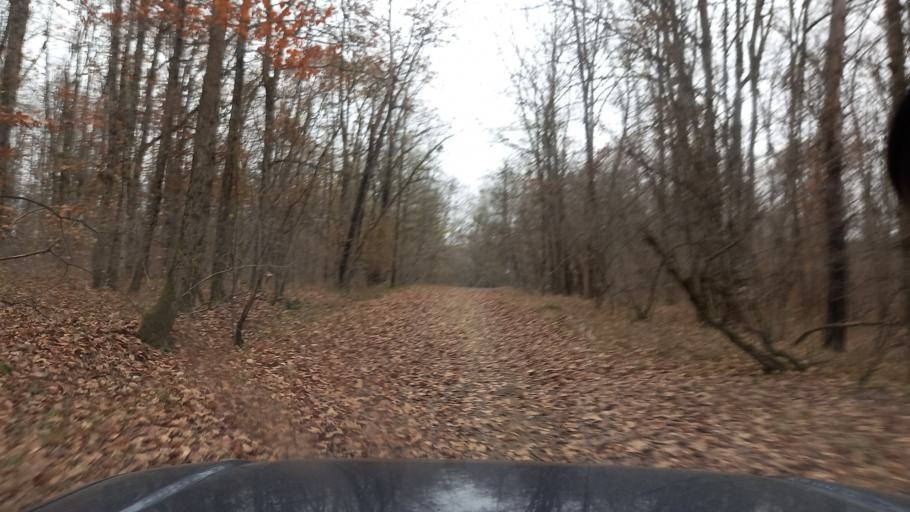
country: RU
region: Krasnodarskiy
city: Goryachiy Klyuch
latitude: 44.5083
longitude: 39.2913
